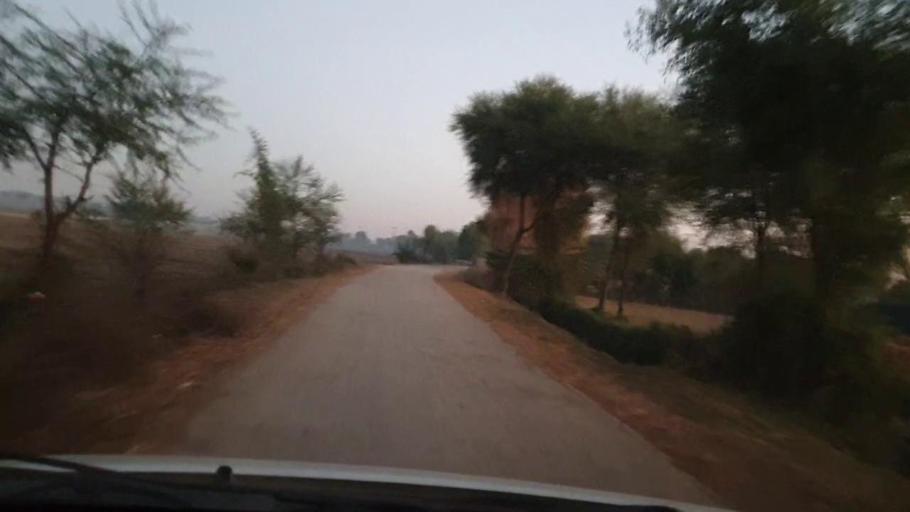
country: PK
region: Sindh
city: Khairpur Nathan Shah
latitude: 27.1369
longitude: 67.7186
